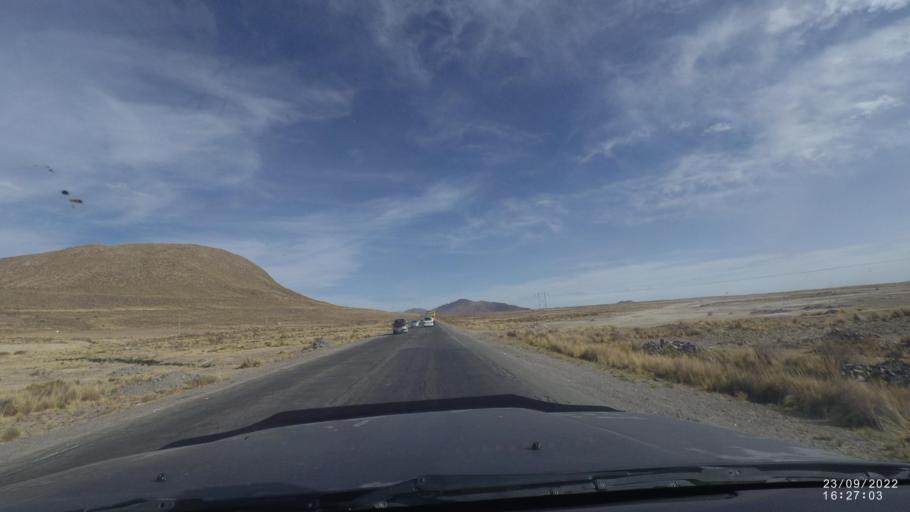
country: BO
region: Oruro
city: Machacamarca
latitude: -18.1125
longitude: -67.0048
